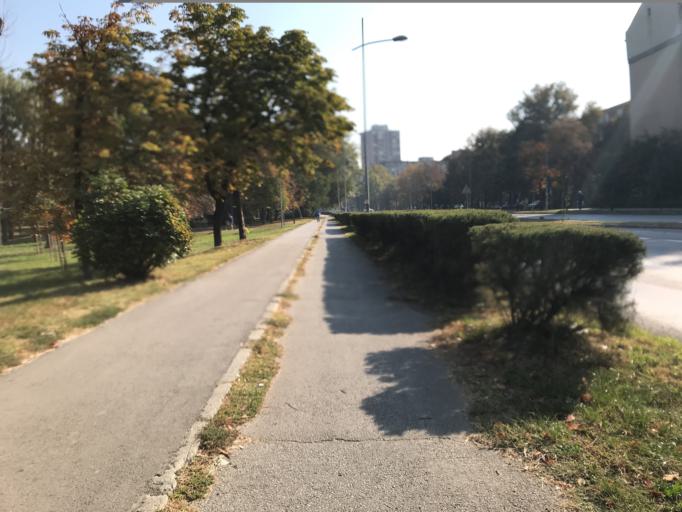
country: RS
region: Autonomna Pokrajina Vojvodina
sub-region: Juznobacki Okrug
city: Novi Sad
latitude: 45.2640
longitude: 19.8245
